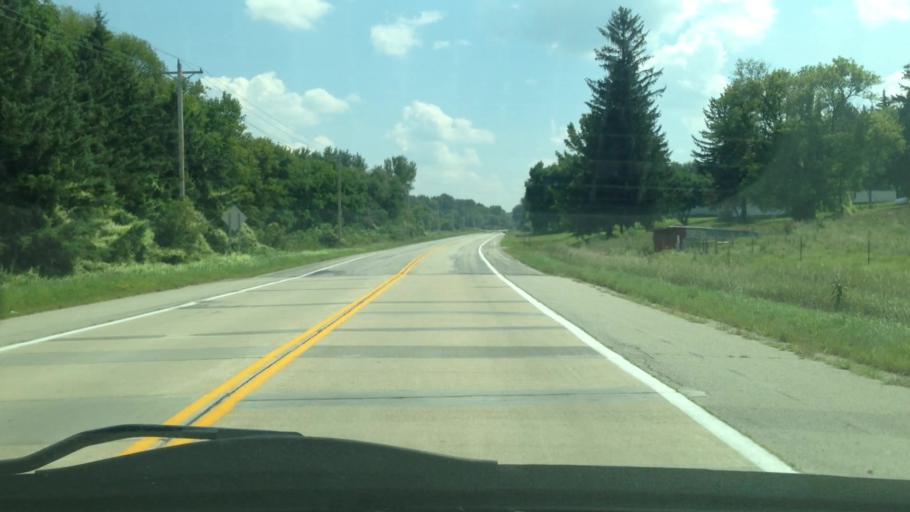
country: US
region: Minnesota
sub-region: Olmsted County
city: Rochester
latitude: 43.9702
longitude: -92.4364
